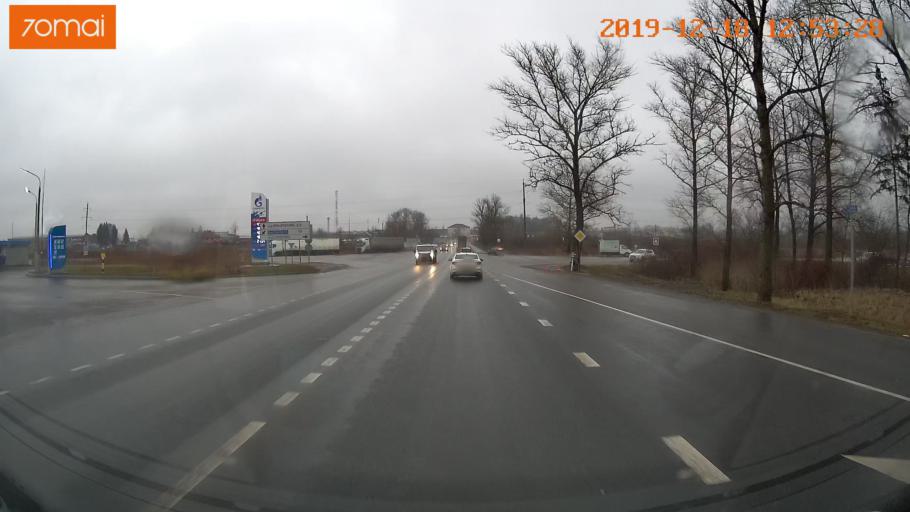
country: RU
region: Moskovskaya
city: Klin
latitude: 56.3193
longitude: 36.6945
